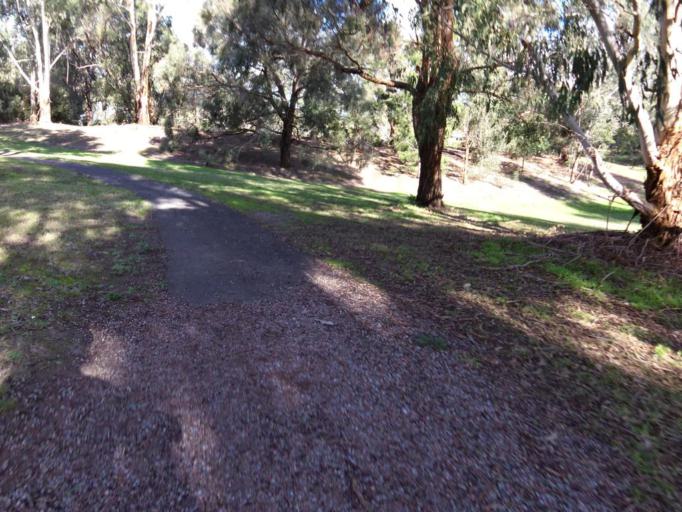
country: AU
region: Victoria
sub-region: Maroondah
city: Croydon Hills
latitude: -37.7724
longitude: 145.2628
